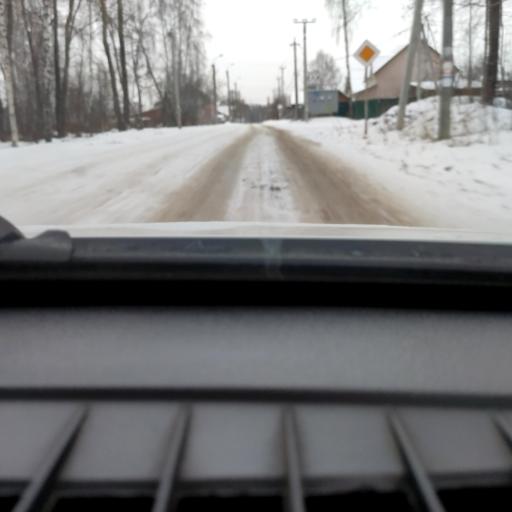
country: RU
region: Perm
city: Perm
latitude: 58.0989
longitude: 56.3672
